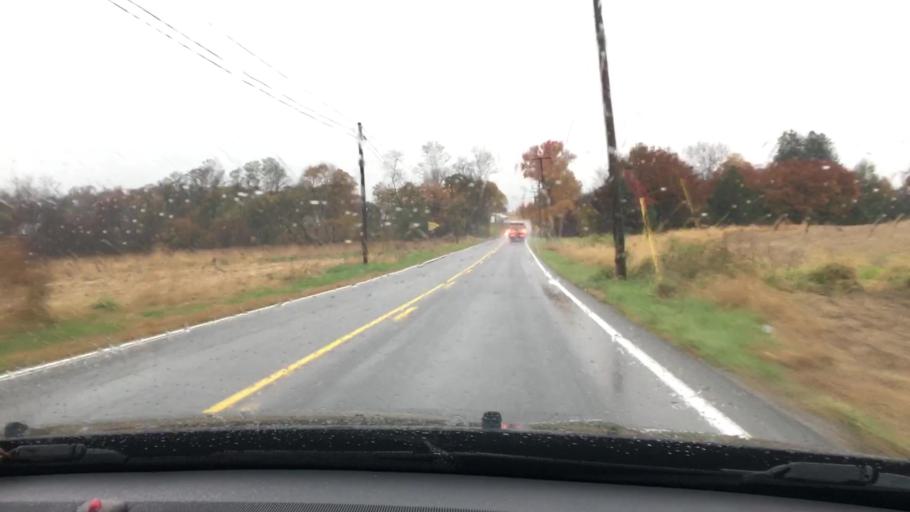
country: US
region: Pennsylvania
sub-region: York County
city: Stewartstown
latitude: 39.7229
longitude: -76.5395
